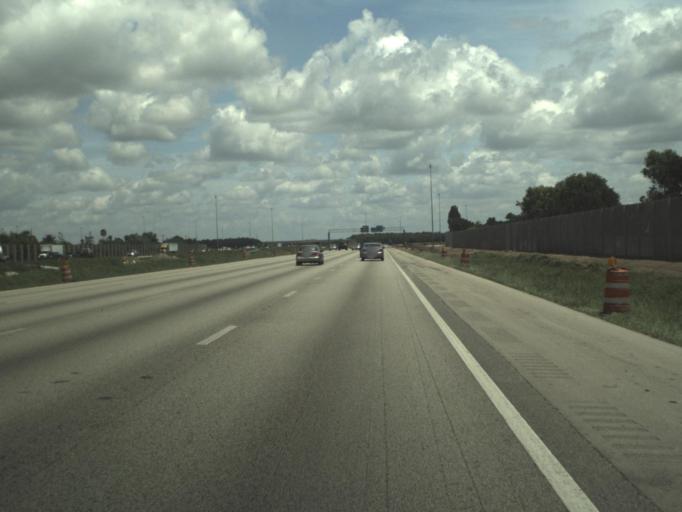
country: US
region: Florida
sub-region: Broward County
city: Southwest Ranches
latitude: 26.0516
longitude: -80.3526
